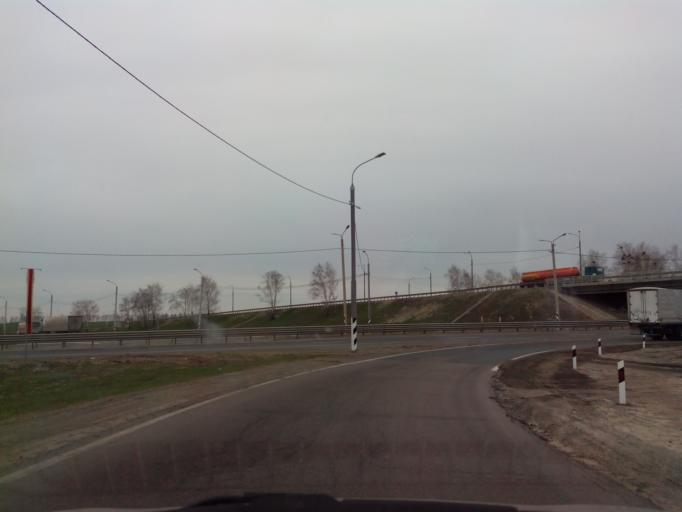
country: RU
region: Tambov
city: Komsomolets
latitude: 52.7339
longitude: 41.2974
